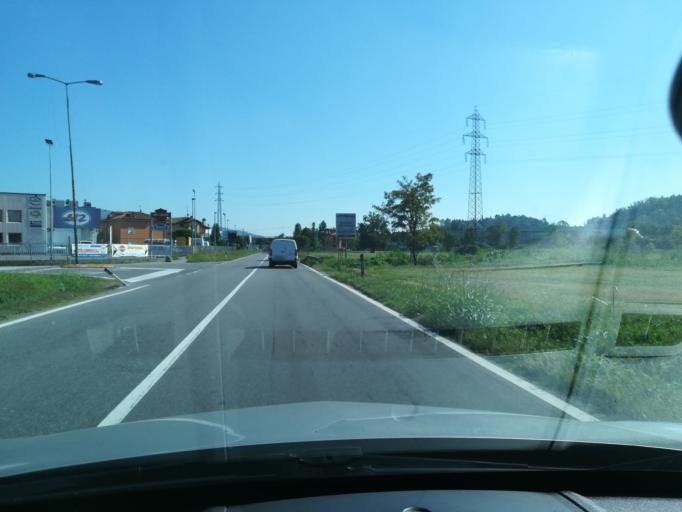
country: IT
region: Lombardy
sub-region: Provincia di Bergamo
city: San Paolo d'Argon
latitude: 45.6799
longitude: 9.7936
